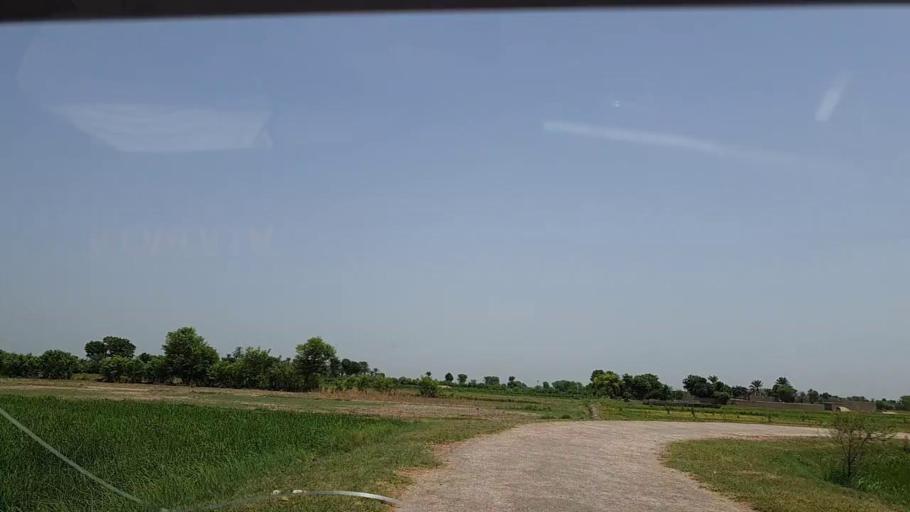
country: PK
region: Sindh
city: Tharu Shah
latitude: 26.9221
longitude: 68.0454
